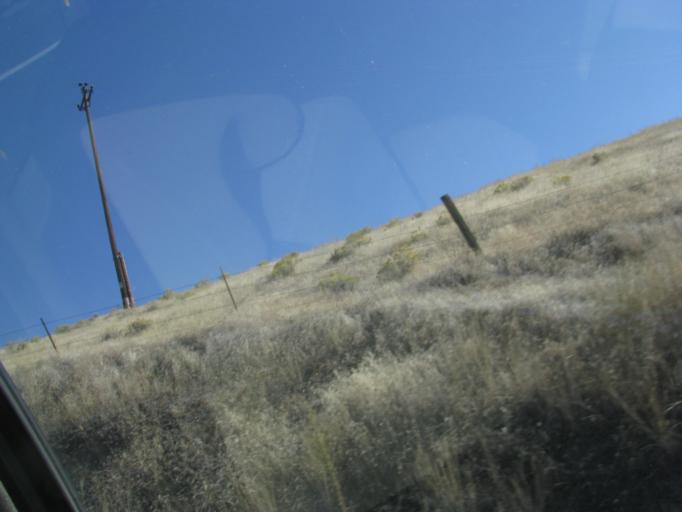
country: US
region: Washington
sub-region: Asotin County
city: Asotin
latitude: 46.3269
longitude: -117.0603
